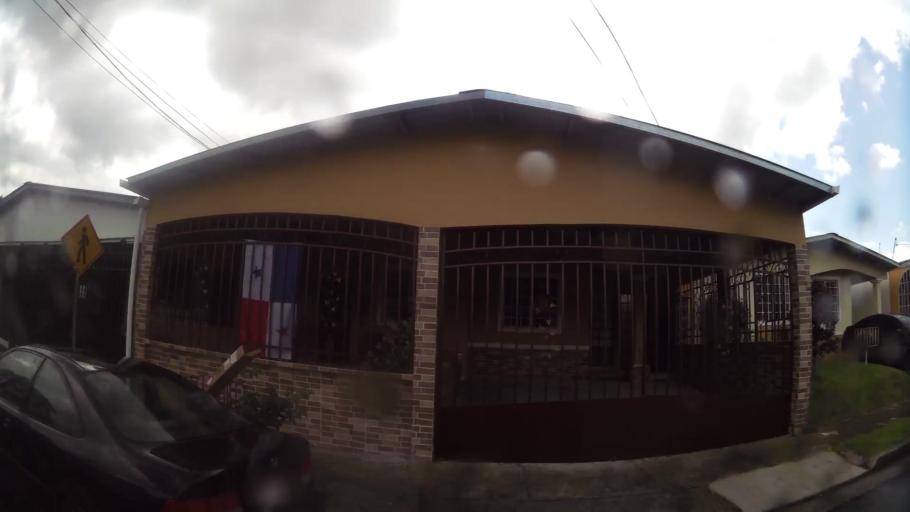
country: PA
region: Panama
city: Nuevo Arraijan
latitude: 8.9401
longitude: -79.7352
